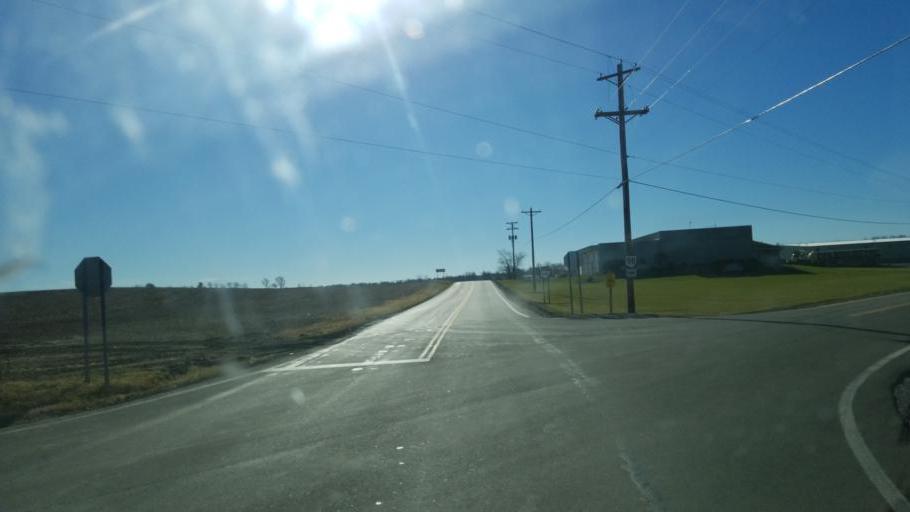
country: US
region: Ohio
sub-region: Huron County
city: Plymouth
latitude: 40.9361
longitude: -82.7267
